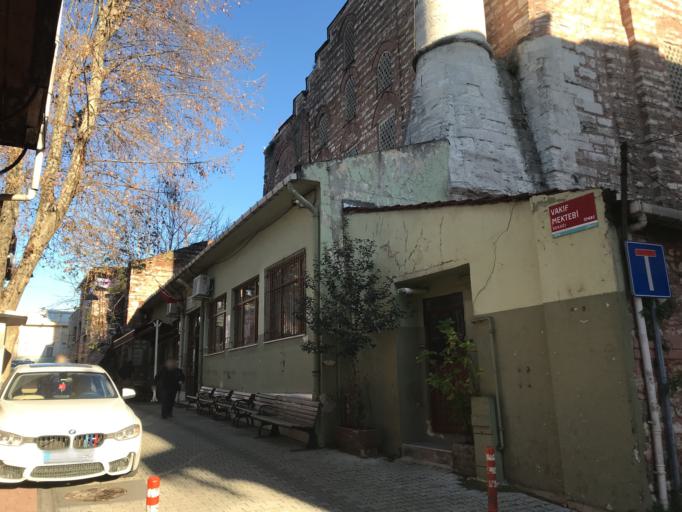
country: TR
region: Istanbul
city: Istanbul
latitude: 41.0269
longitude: 28.9560
